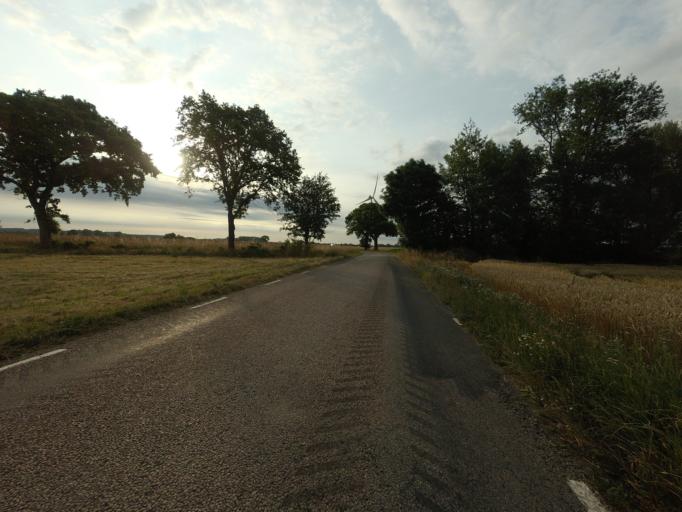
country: SE
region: Skane
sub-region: Helsingborg
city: Odakra
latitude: 56.1496
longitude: 12.6558
